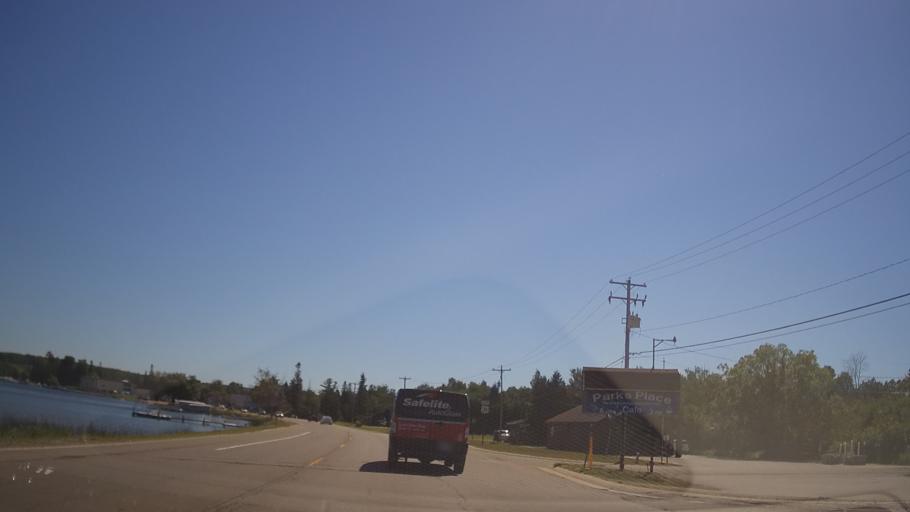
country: US
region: Michigan
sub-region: Emmet County
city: Petoskey
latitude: 45.4214
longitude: -84.8629
